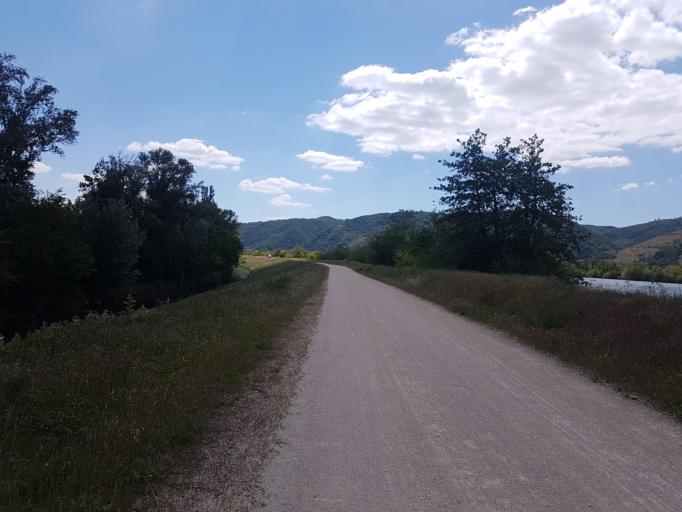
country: FR
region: Rhone-Alpes
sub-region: Departement de l'Ardeche
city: Mauves
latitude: 45.0371
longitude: 4.8441
